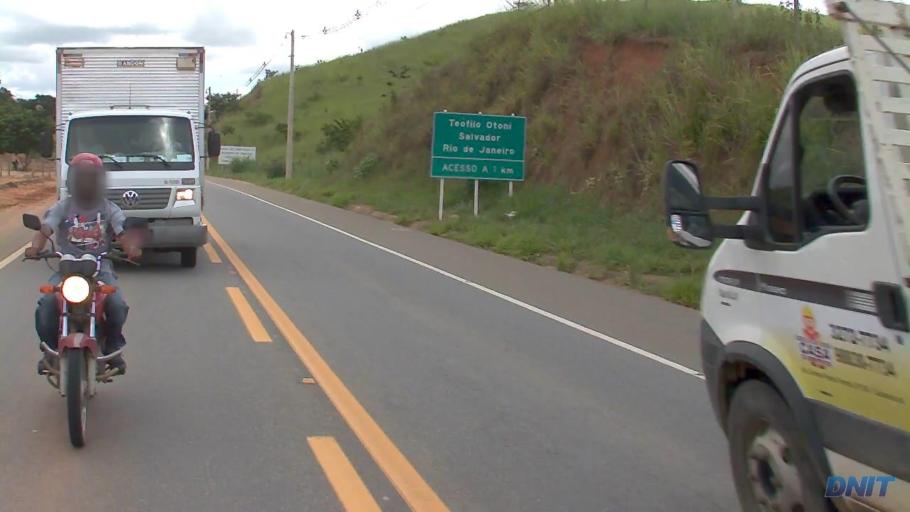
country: BR
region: Minas Gerais
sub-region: Governador Valadares
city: Governador Valadares
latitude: -18.8765
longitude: -41.9932
